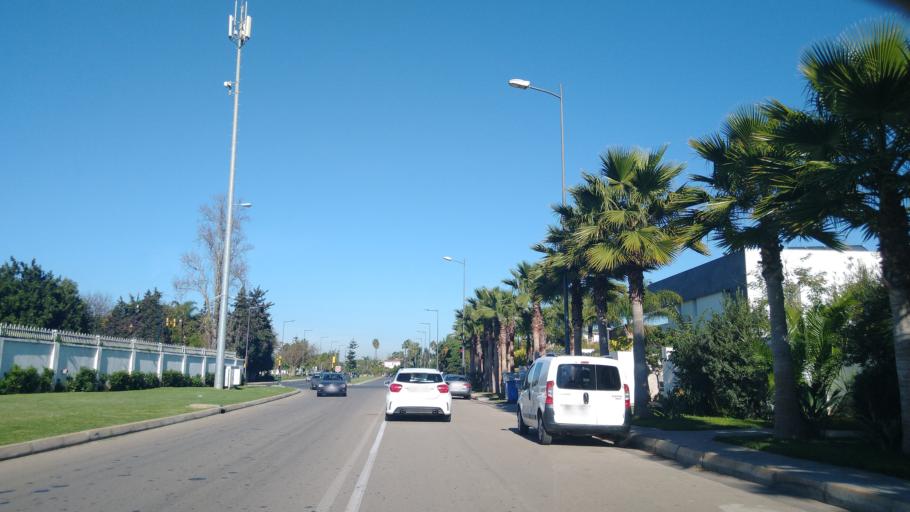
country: MA
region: Rabat-Sale-Zemmour-Zaer
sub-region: Rabat
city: Rabat
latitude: 33.9588
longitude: -6.8419
